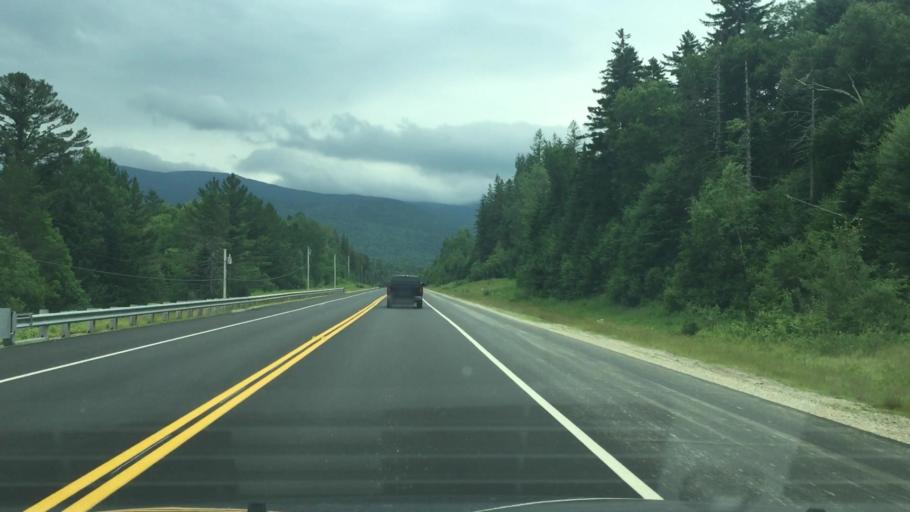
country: US
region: New Hampshire
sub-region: Coos County
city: Jefferson
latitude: 44.2505
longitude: -71.4421
